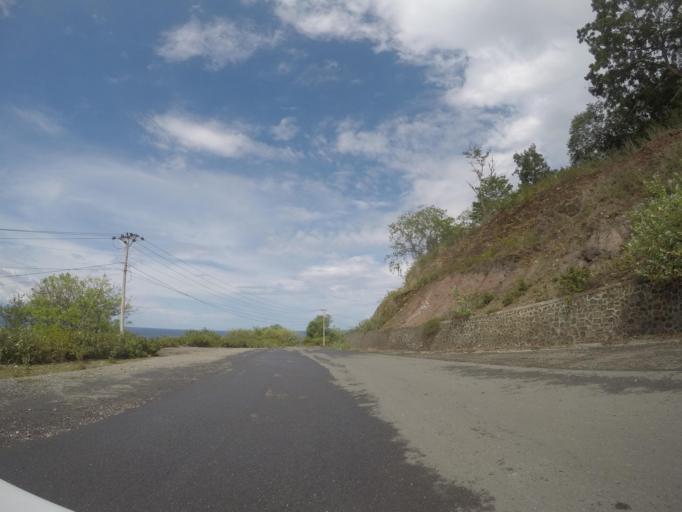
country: TL
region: Liquica
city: Maubara
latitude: -8.6338
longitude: 125.1464
